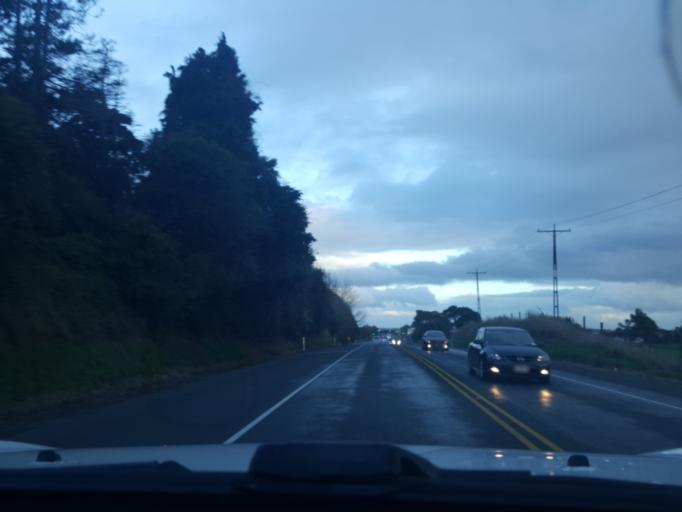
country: NZ
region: Waikato
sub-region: Waikato District
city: Ngaruawahia
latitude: -37.7240
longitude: 175.2176
